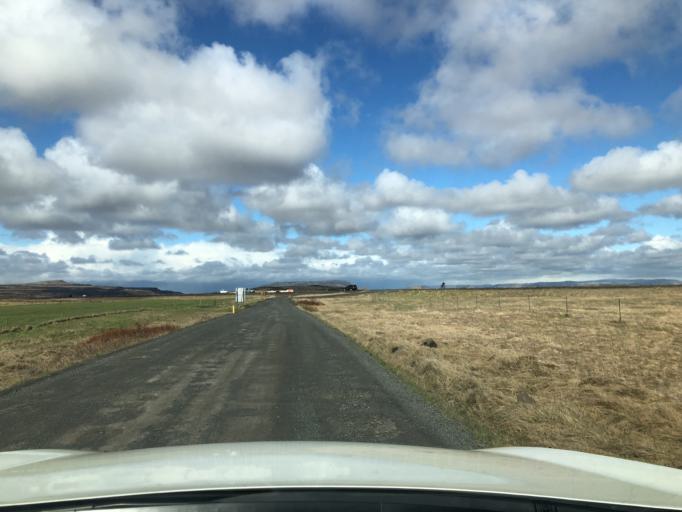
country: IS
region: South
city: Selfoss
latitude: 63.9313
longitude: -20.6696
